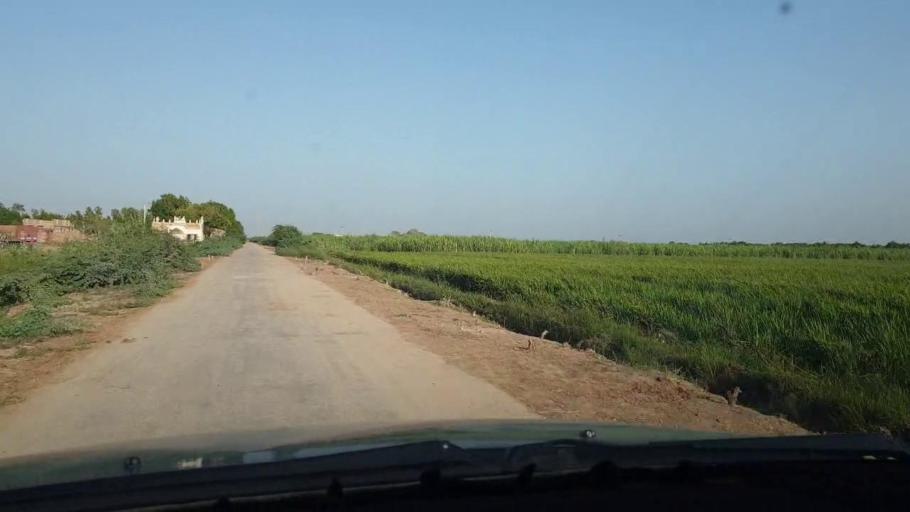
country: PK
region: Sindh
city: Mirwah Gorchani
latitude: 25.2996
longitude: 68.9660
